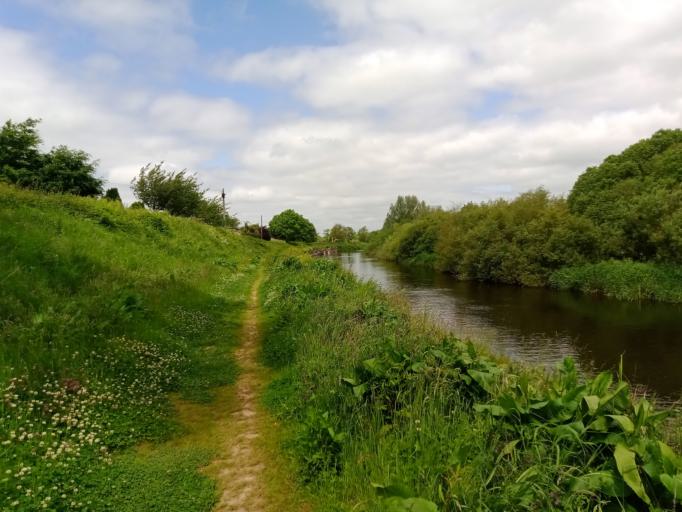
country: IE
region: Leinster
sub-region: County Carlow
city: Carlow
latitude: 52.8052
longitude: -6.9664
